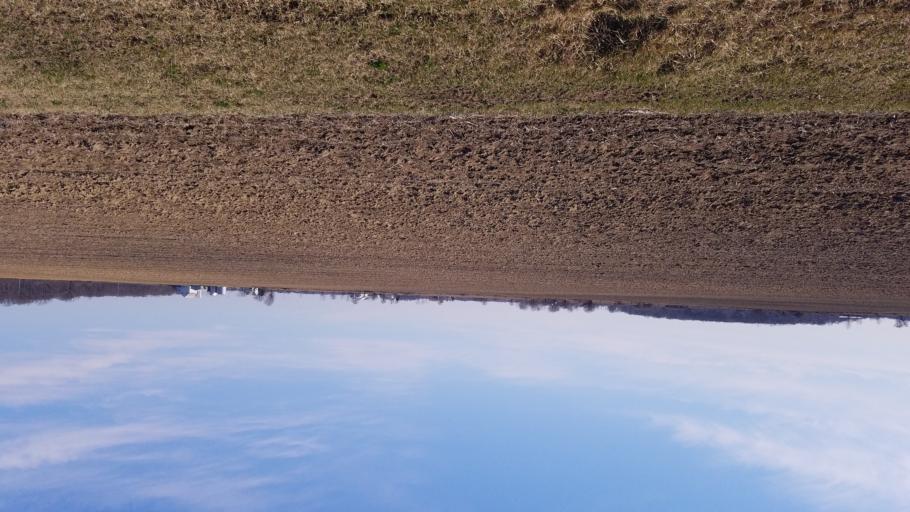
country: US
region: Ohio
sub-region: Hardin County
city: Kenton
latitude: 40.5386
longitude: -83.4565
